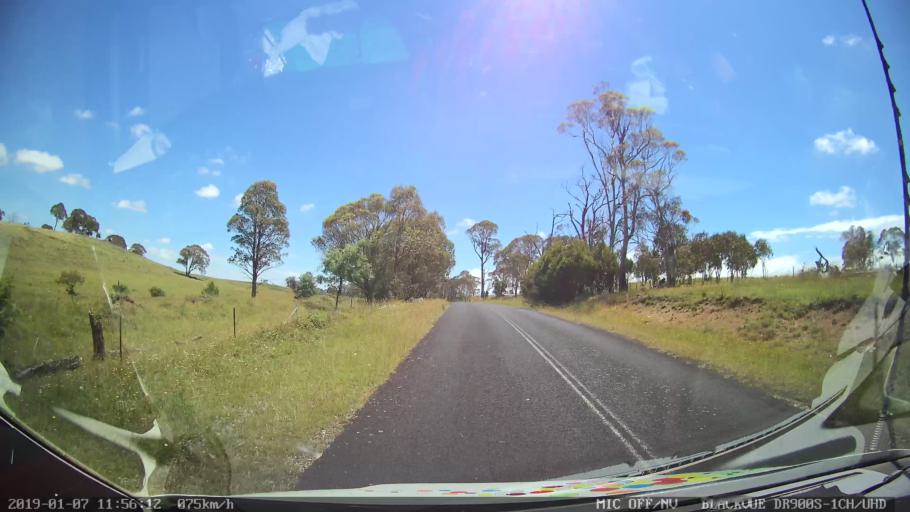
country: AU
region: New South Wales
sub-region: Guyra
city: Guyra
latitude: -30.2772
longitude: 151.6740
